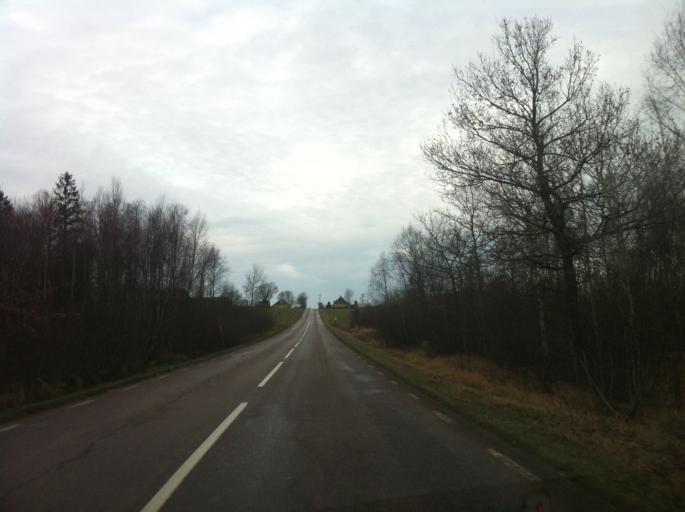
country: SE
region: Skane
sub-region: Svalovs Kommun
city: Kagerod
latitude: 56.0414
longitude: 13.1025
